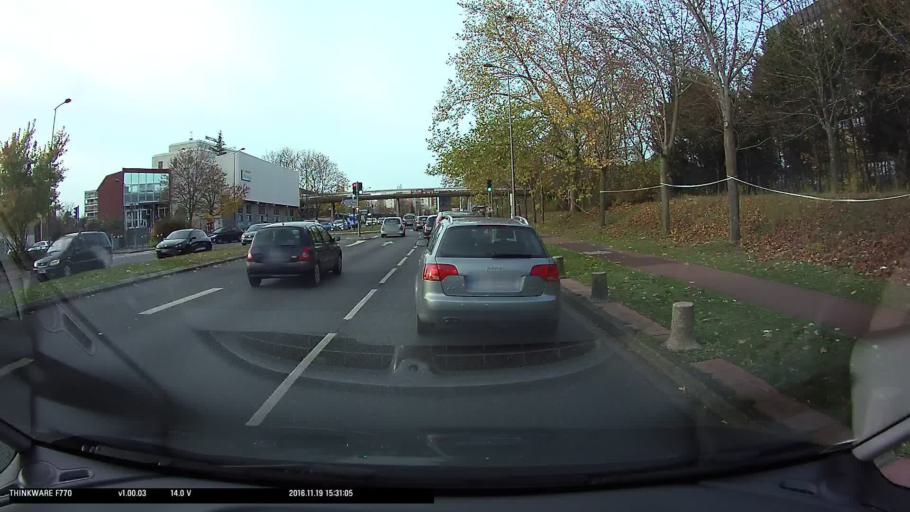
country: FR
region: Ile-de-France
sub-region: Departement du Val-d'Oise
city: Cergy-Pontoise
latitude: 49.0407
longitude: 2.0746
